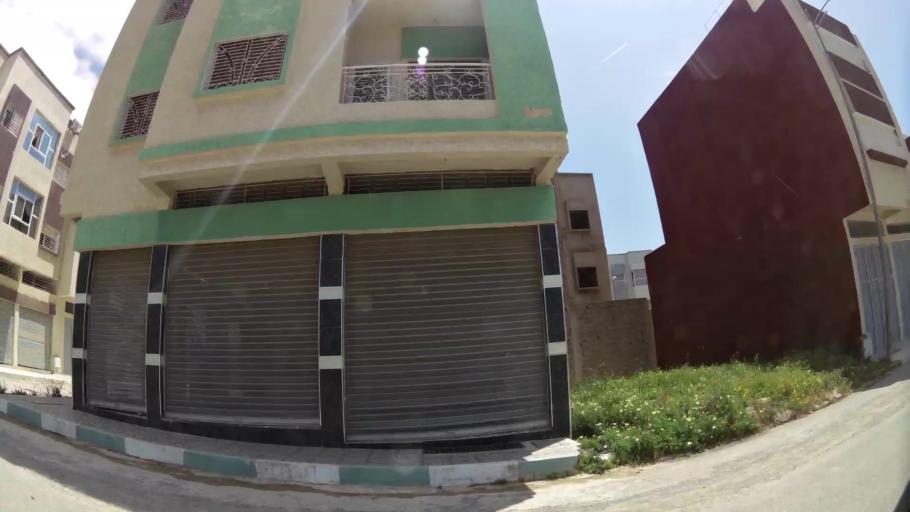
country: MA
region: Fes-Boulemane
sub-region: Fes
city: Fes
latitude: 34.0558
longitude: -5.0424
